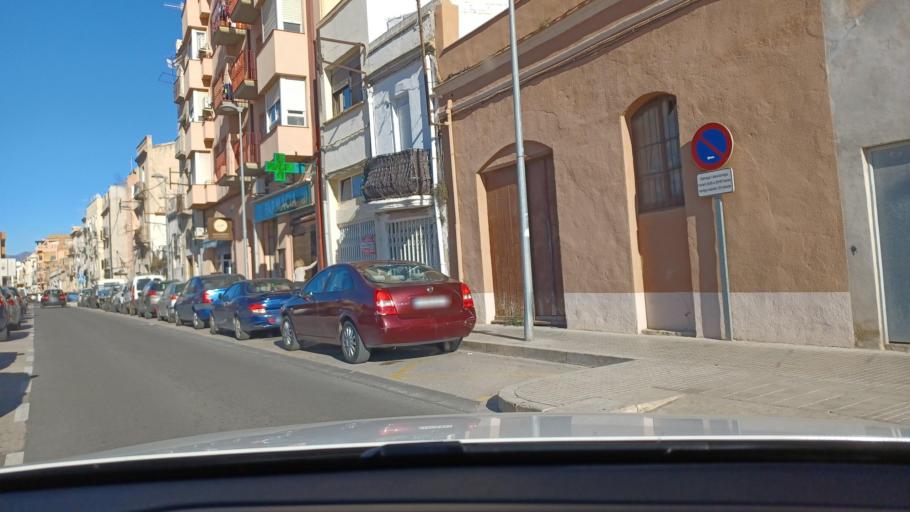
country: ES
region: Catalonia
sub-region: Provincia de Tarragona
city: Tortosa
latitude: 40.8152
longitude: 0.5219
